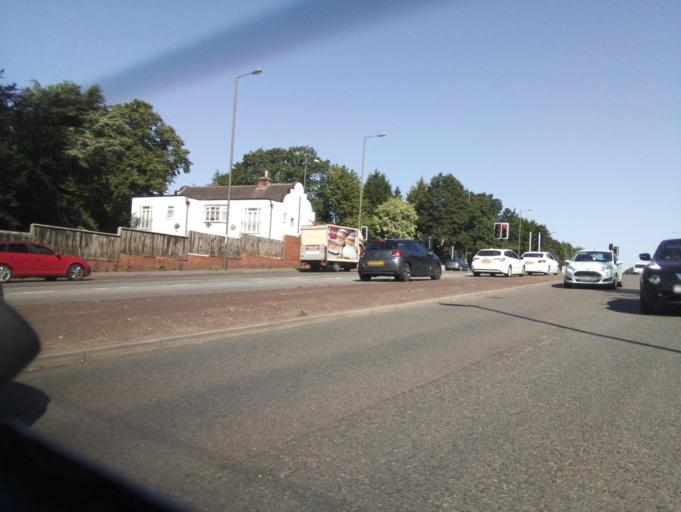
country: GB
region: England
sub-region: Derby
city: Derby
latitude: 52.9075
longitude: -1.5007
